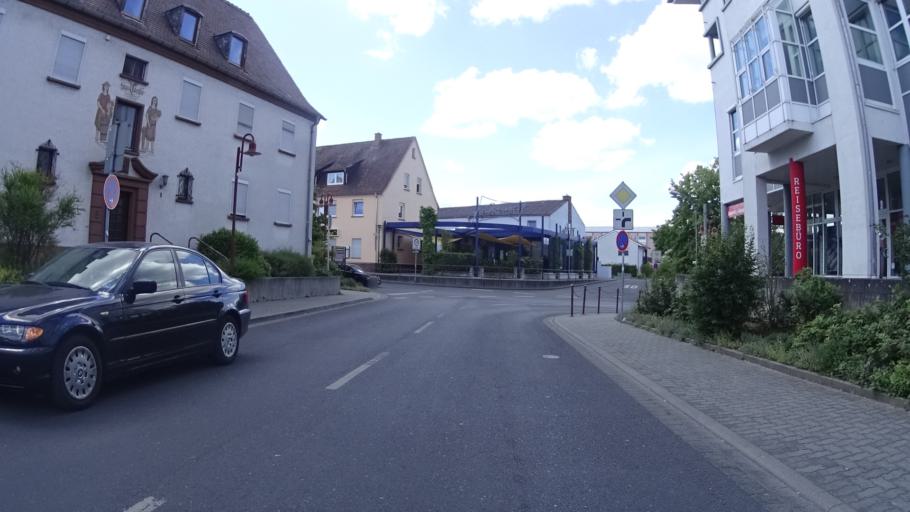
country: DE
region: Bavaria
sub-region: Regierungsbezirk Unterfranken
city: Worth am Main
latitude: 49.8036
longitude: 9.1551
